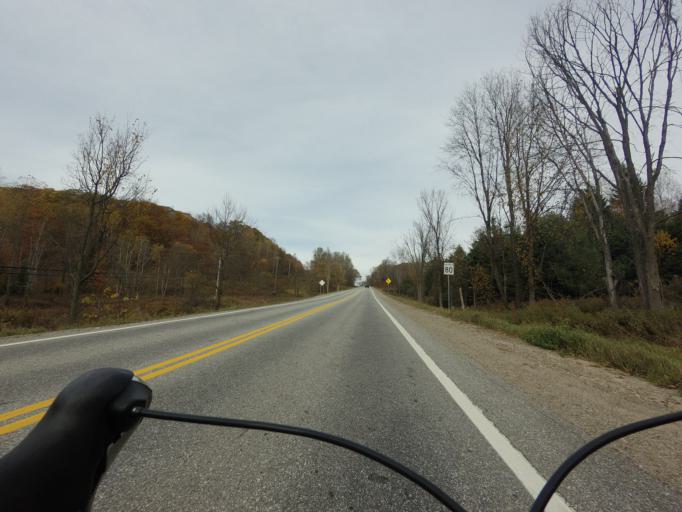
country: CA
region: Quebec
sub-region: Outaouais
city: Val-des-Monts
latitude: 45.6705
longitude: -75.7328
